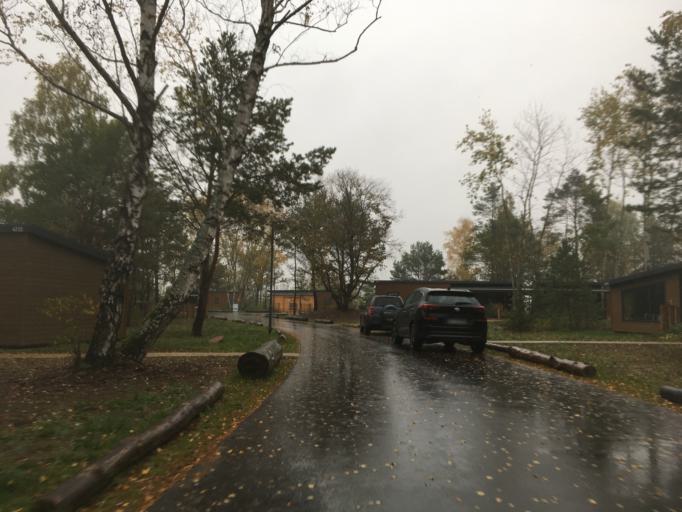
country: DE
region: Brandenburg
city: Halbe
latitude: 52.0341
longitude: 13.7368
